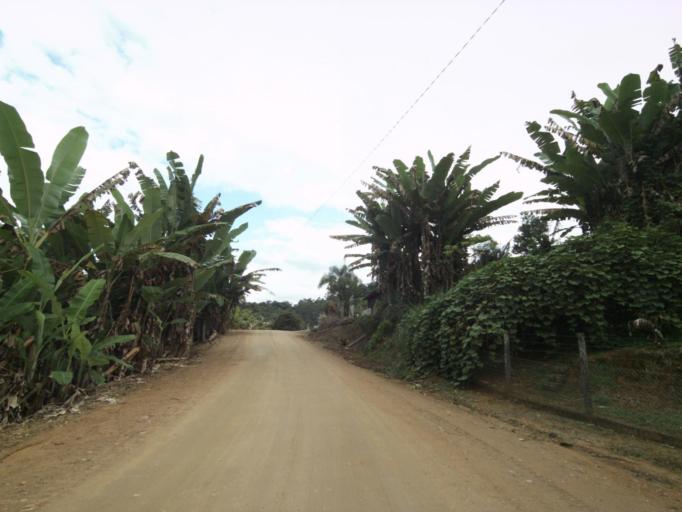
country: BR
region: Santa Catarina
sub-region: Pomerode
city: Pomerode
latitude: -26.7022
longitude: -49.2258
